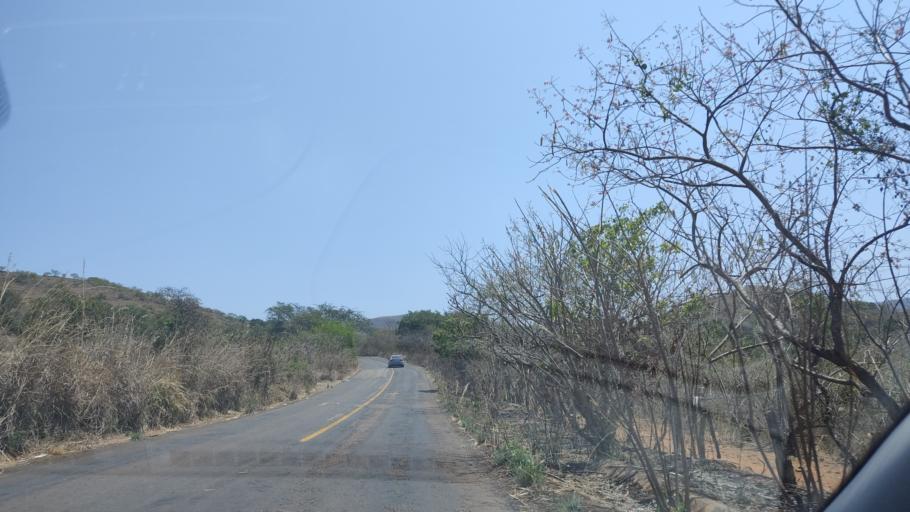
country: MX
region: Nayarit
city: Puga
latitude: 21.5784
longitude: -104.7671
